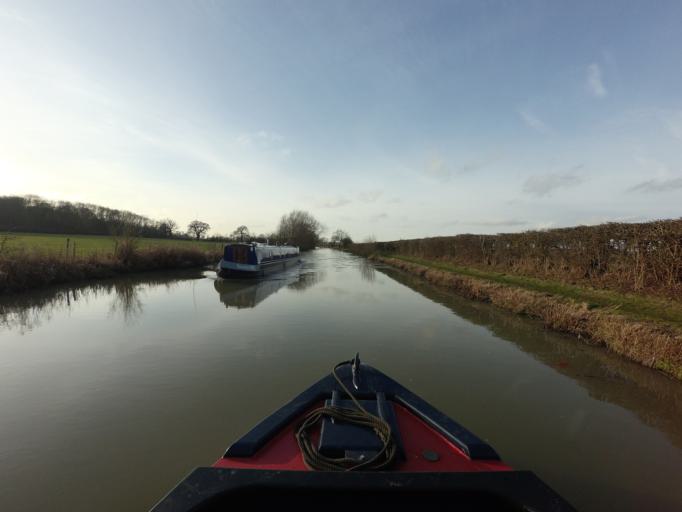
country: GB
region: England
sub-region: Northamptonshire
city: Bugbrooke
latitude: 52.2010
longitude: -0.9913
